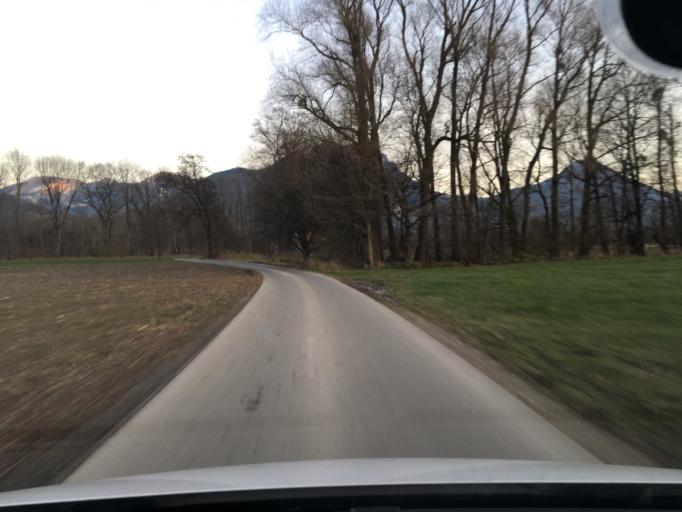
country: DE
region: Bavaria
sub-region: Upper Bavaria
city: Flintsbach
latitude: 47.7462
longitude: 12.1261
